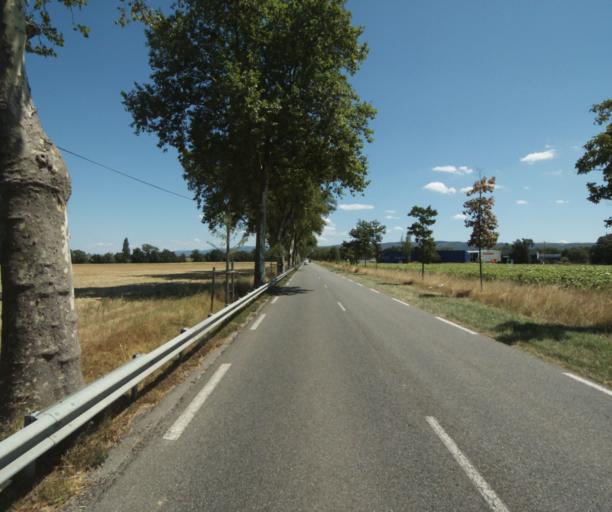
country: FR
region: Midi-Pyrenees
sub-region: Departement de la Haute-Garonne
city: Saint-Felix-Lauragais
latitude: 43.4467
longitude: 1.9393
